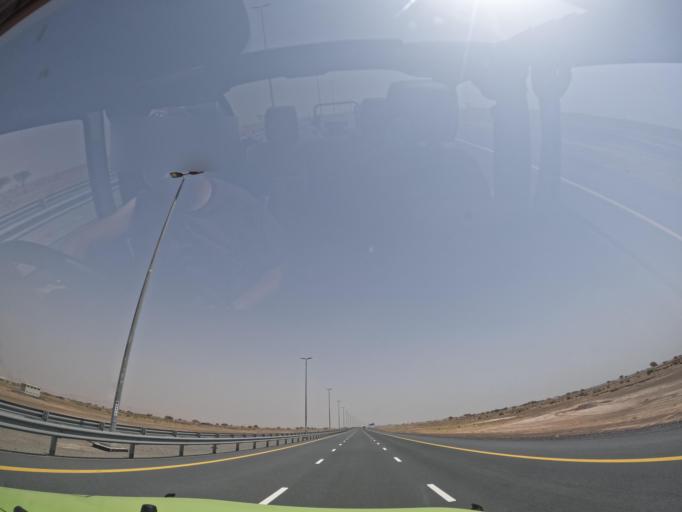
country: AE
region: Ash Shariqah
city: Adh Dhayd
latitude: 24.9972
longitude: 55.8611
